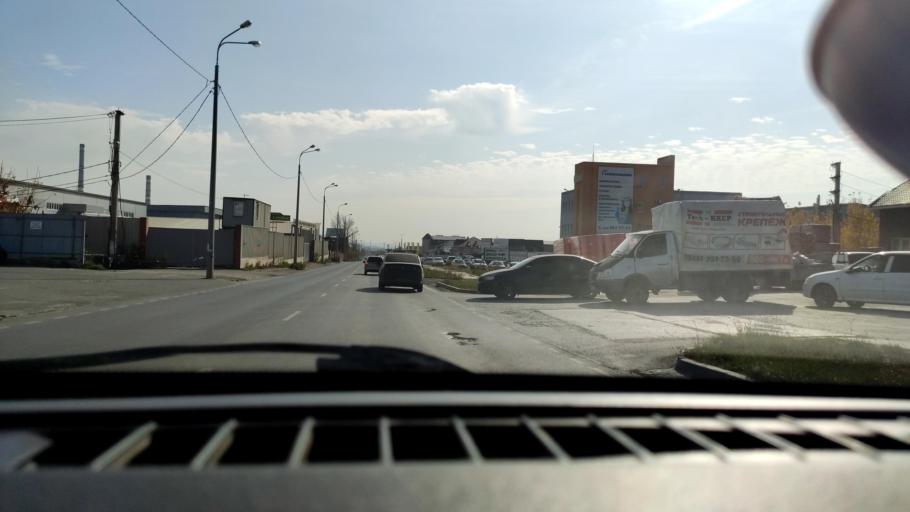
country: RU
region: Samara
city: Petra-Dubrava
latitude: 53.2638
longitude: 50.2617
